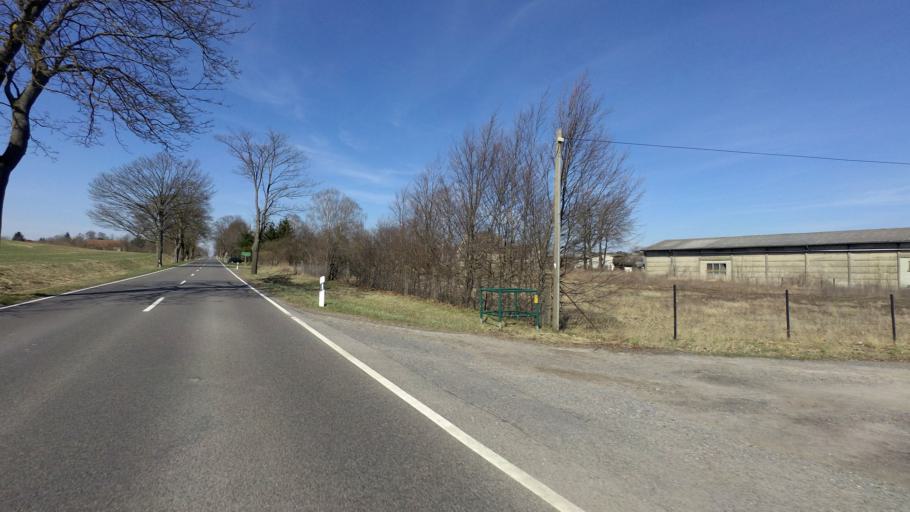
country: DE
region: Brandenburg
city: Buckow
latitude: 52.5947
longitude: 14.0264
